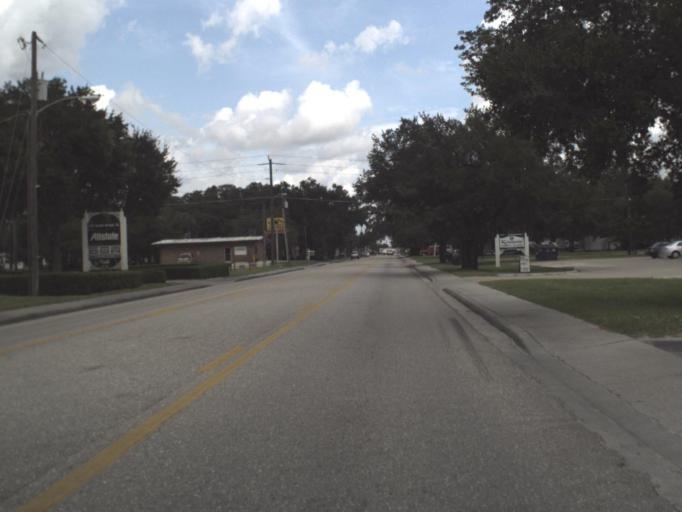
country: US
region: Florida
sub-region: Hendry County
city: LaBelle
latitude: 26.7579
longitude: -81.4373
